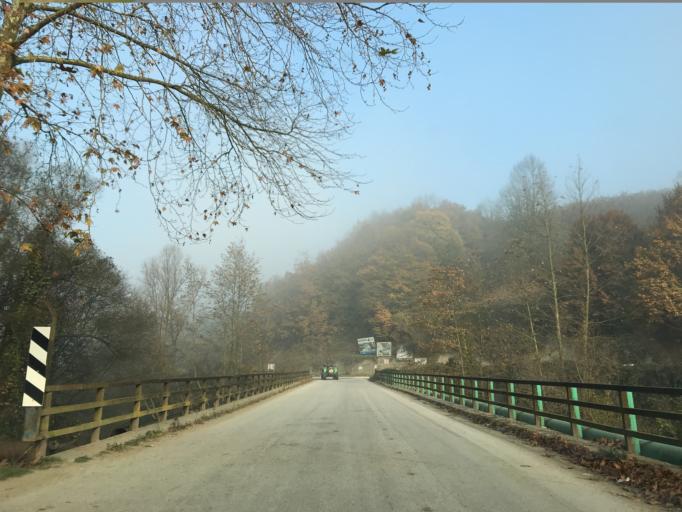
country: TR
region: Duzce
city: Cumayeri
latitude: 40.8944
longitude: 30.9563
